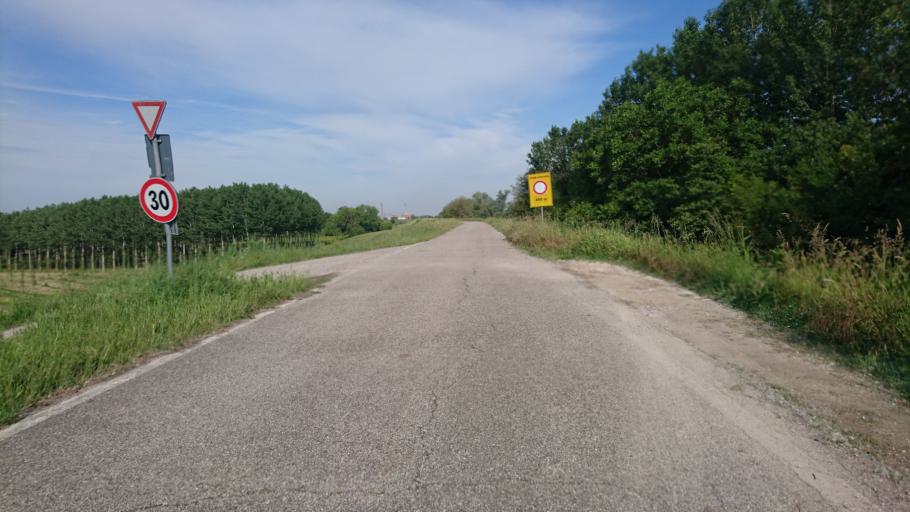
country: IT
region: Veneto
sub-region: Provincia di Rovigo
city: Castelnovo Bariano
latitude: 45.0153
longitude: 11.2783
